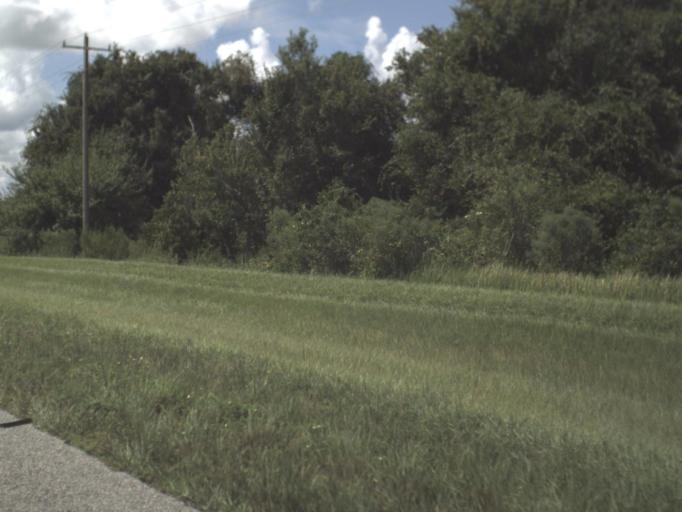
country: US
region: Florida
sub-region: DeSoto County
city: Arcadia
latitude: 27.3232
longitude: -81.8133
